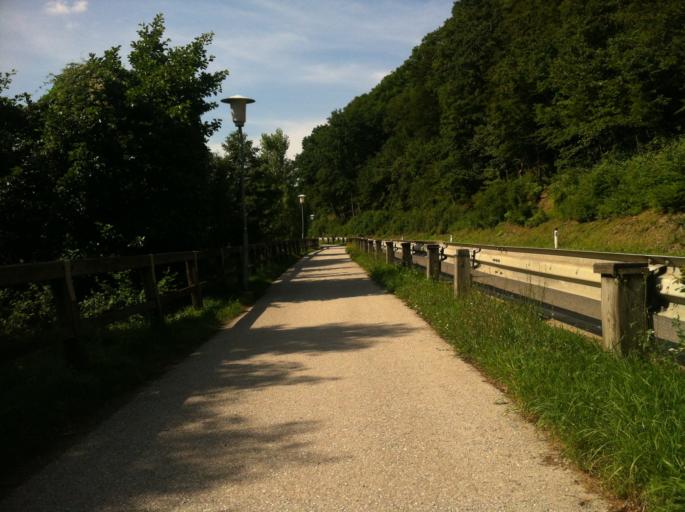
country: AT
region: Lower Austria
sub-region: Politischer Bezirk Wien-Umgebung
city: Wolfsgraben
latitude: 48.1776
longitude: 16.1233
